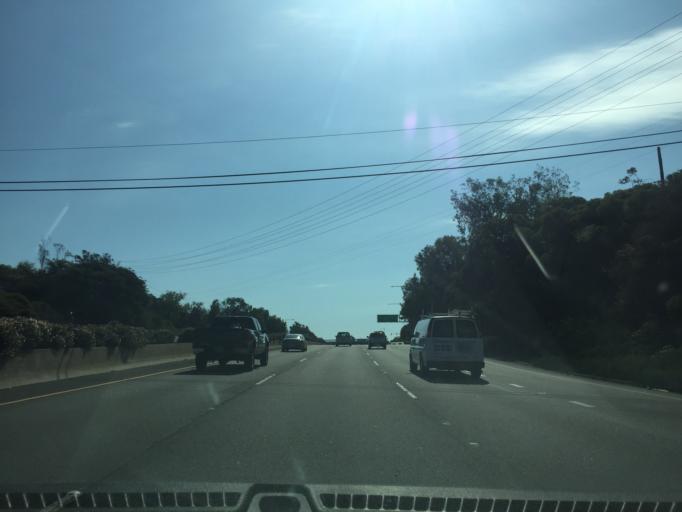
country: US
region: California
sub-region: Santa Barbara County
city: Mission Canyon
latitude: 34.4398
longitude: -119.7552
